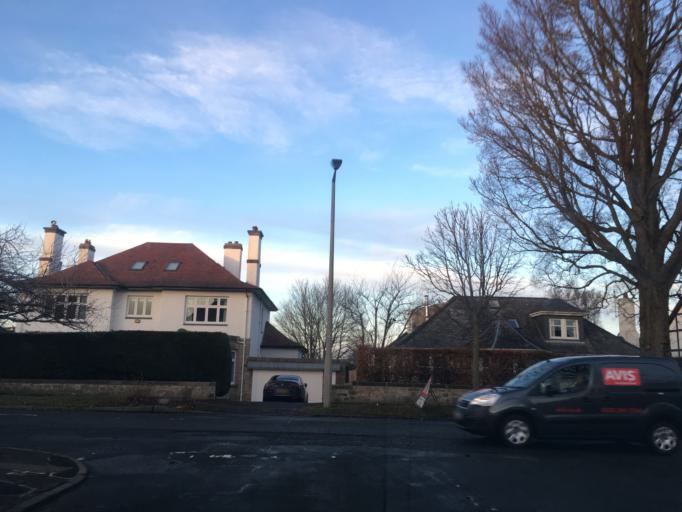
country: GB
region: Scotland
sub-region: Edinburgh
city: Colinton
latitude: 55.9506
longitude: -3.2446
